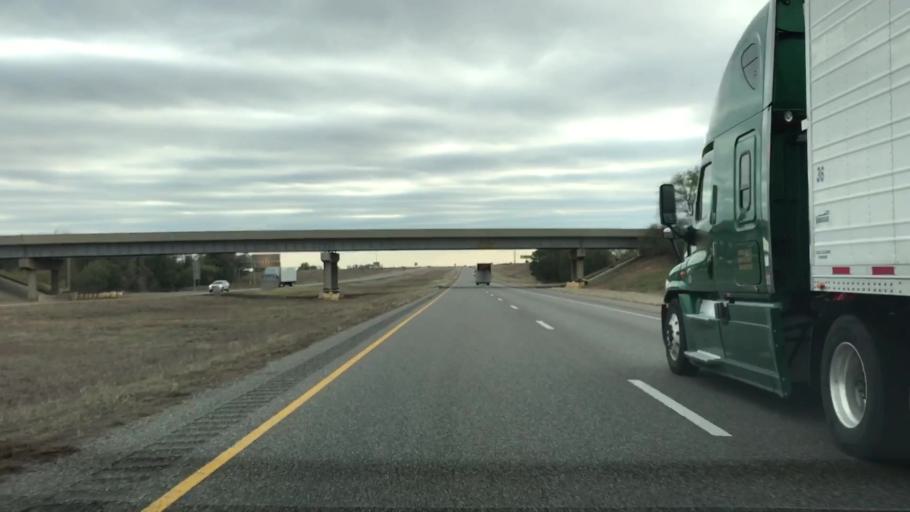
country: US
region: Oklahoma
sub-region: Beckham County
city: Sayre
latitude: 35.3065
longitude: -99.6158
